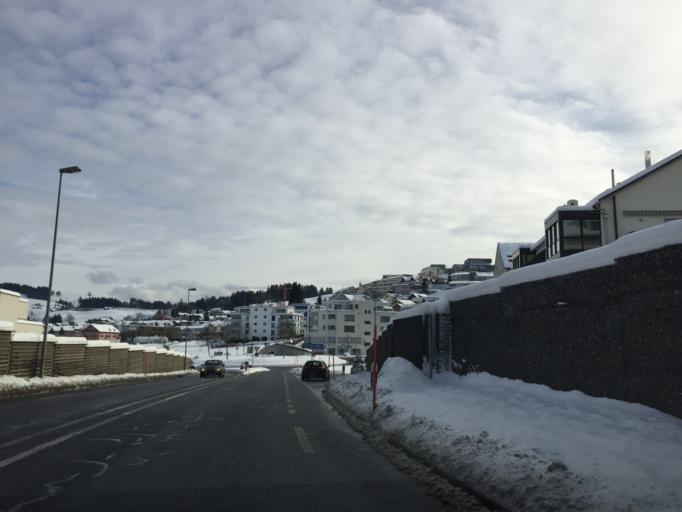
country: CH
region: Schwyz
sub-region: Bezirk Hoefe
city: Schindellegi
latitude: 47.1771
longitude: 8.7109
